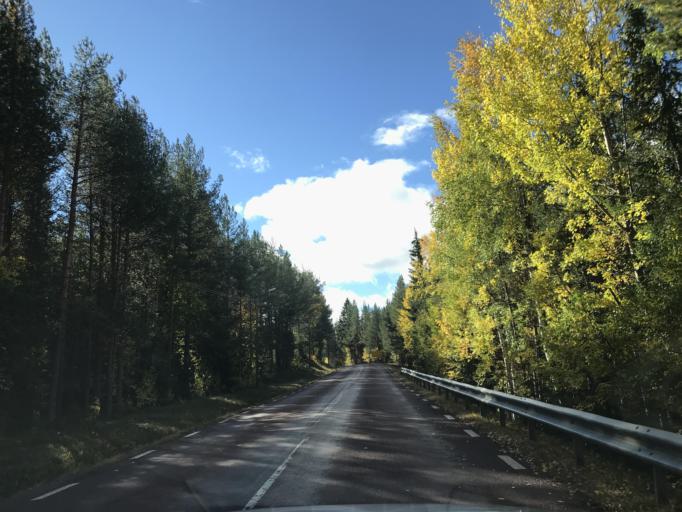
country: NO
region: Hedmark
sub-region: Trysil
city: Innbygda
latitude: 61.6861
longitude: 13.1292
